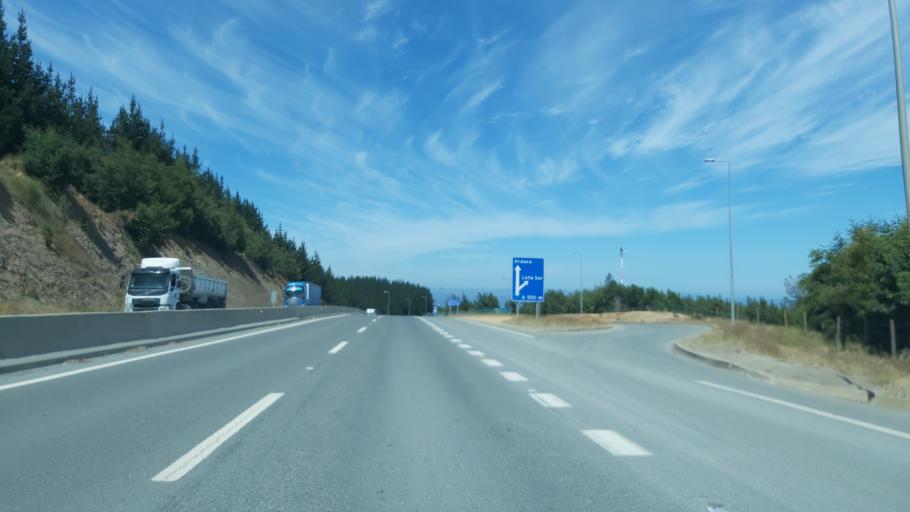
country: CL
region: Biobio
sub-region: Provincia de Concepcion
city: Lota
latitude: -37.0975
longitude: -73.1418
